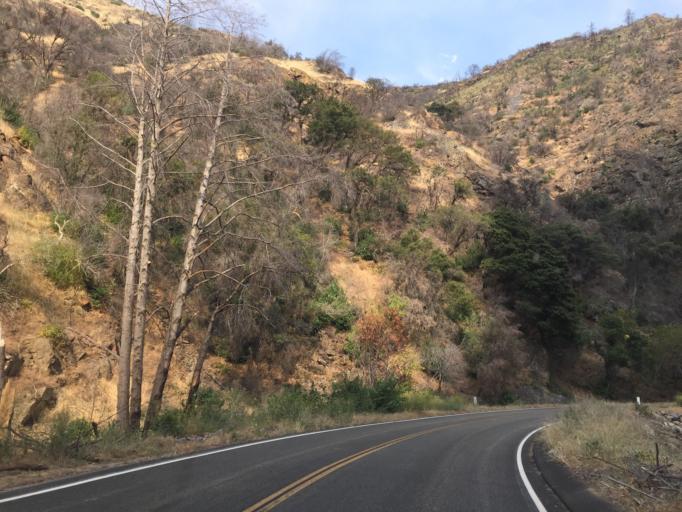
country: US
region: California
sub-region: Tulare County
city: Three Rivers
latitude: 36.8155
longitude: -118.8167
